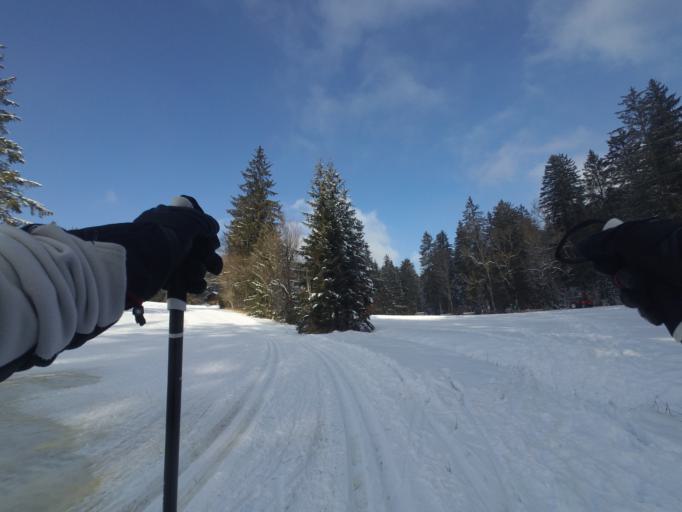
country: AT
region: Salzburg
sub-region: Politischer Bezirk Salzburg-Umgebung
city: Thalgau
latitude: 47.8770
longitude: 13.2574
